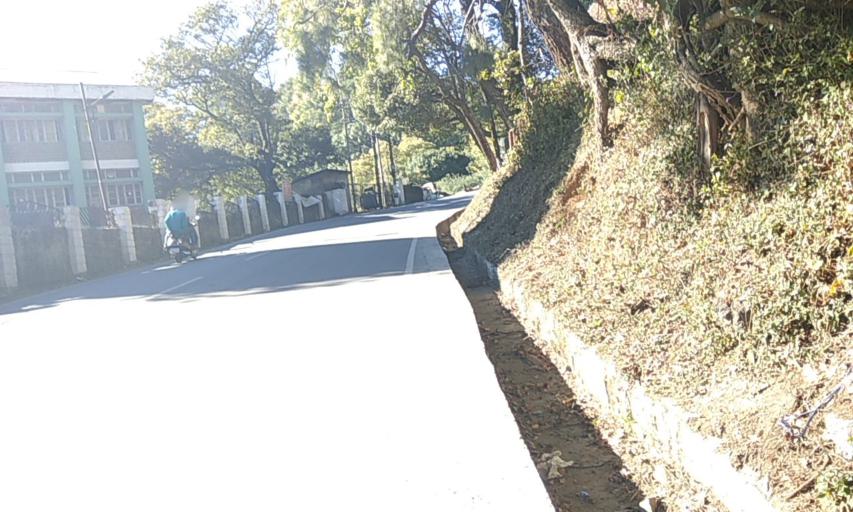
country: IN
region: Himachal Pradesh
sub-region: Kangra
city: Dharmsala
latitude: 32.2136
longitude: 76.3195
